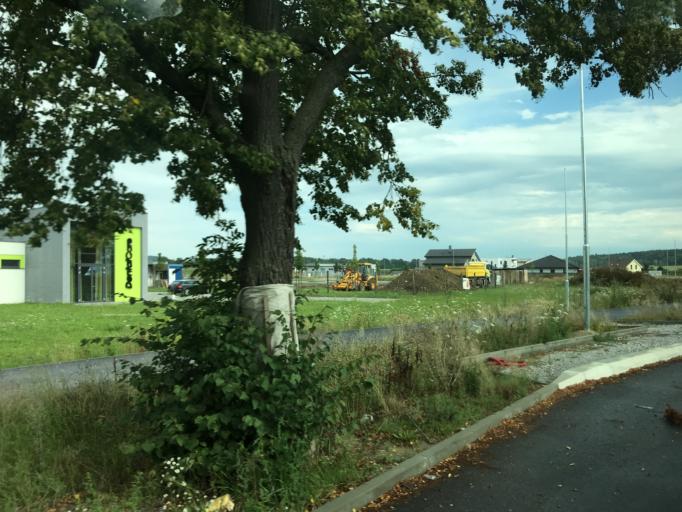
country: CZ
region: Jihocesky
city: Vcelna
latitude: 48.9395
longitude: 14.4641
